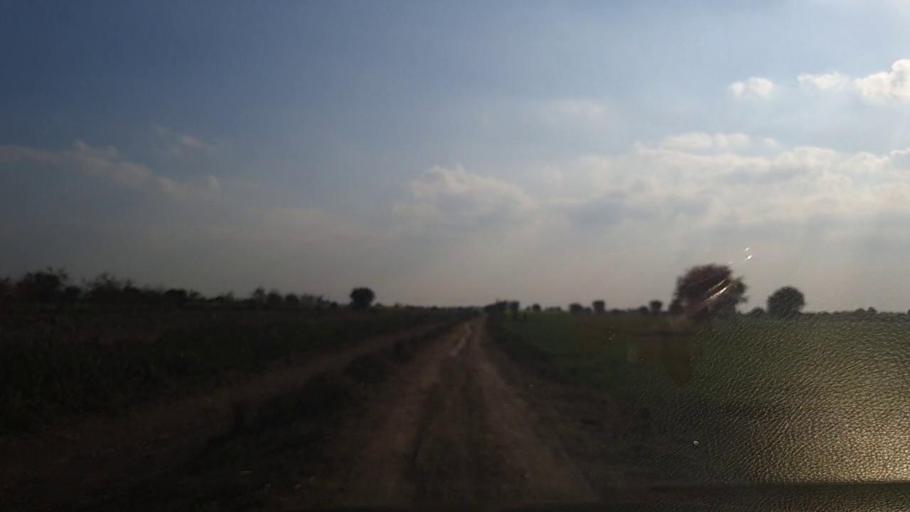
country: PK
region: Sindh
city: Jhol
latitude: 25.8310
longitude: 69.0511
